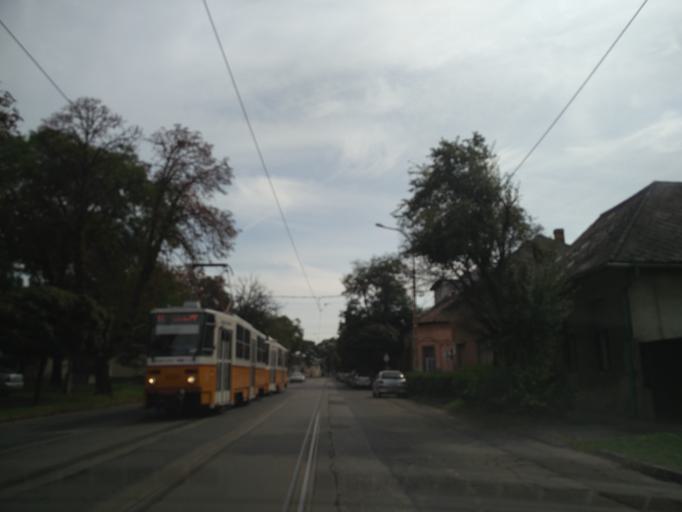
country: HU
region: Budapest
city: Budapest XV. keruelet
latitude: 47.5677
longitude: 19.1199
